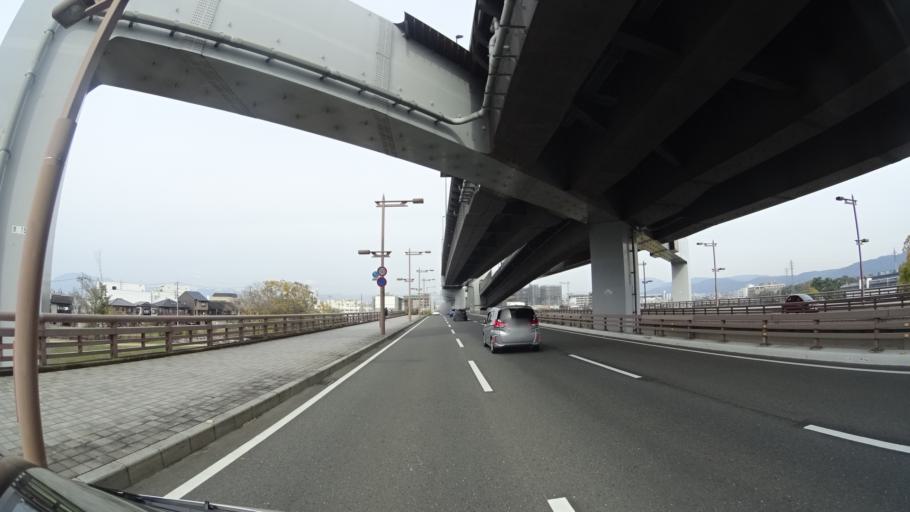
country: JP
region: Kyoto
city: Muko
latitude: 34.9600
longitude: 135.7525
